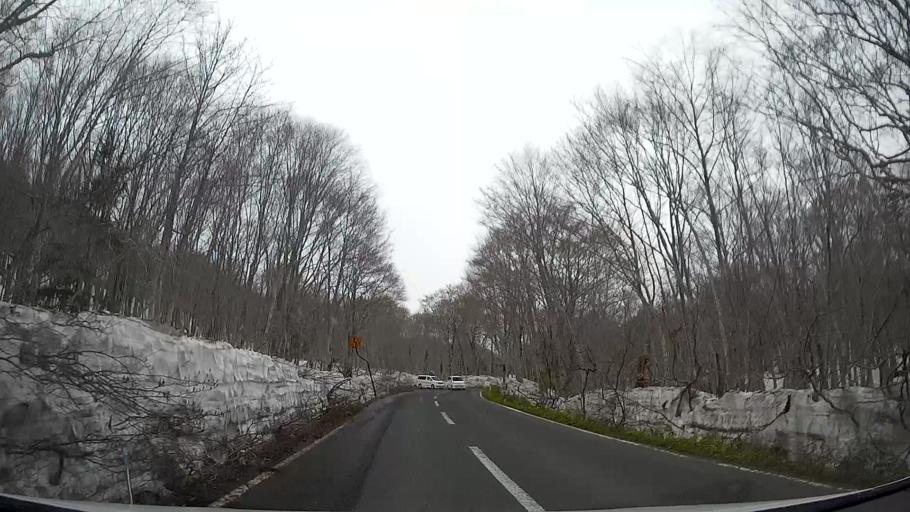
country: JP
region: Aomori
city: Aomori Shi
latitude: 40.6300
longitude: 140.9208
